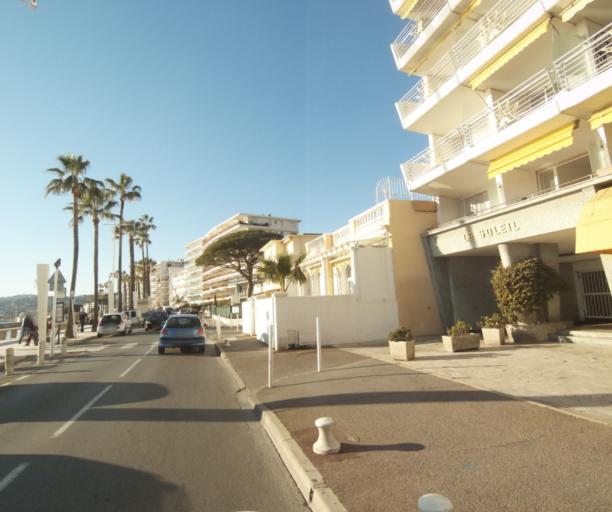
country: FR
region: Provence-Alpes-Cote d'Azur
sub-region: Departement des Alpes-Maritimes
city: Antibes
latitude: 43.5700
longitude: 7.1059
